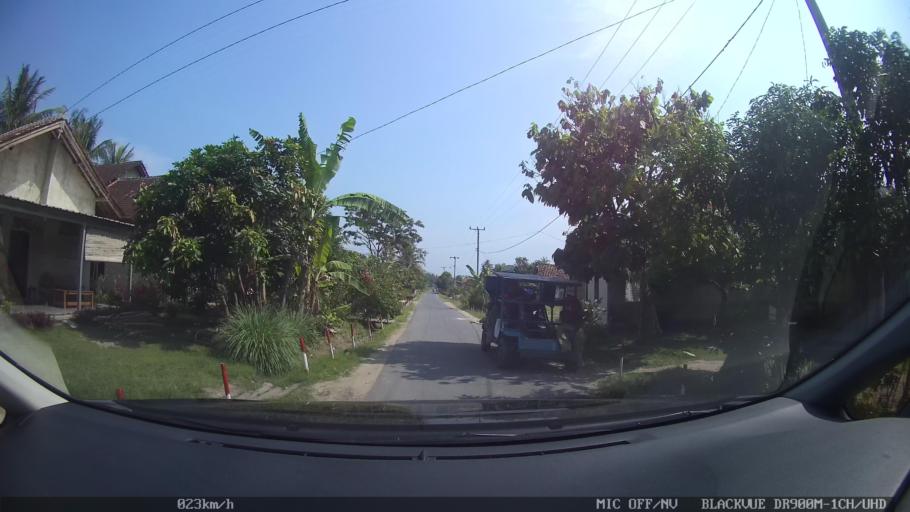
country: ID
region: Lampung
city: Natar
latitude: -5.2612
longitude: 105.2128
